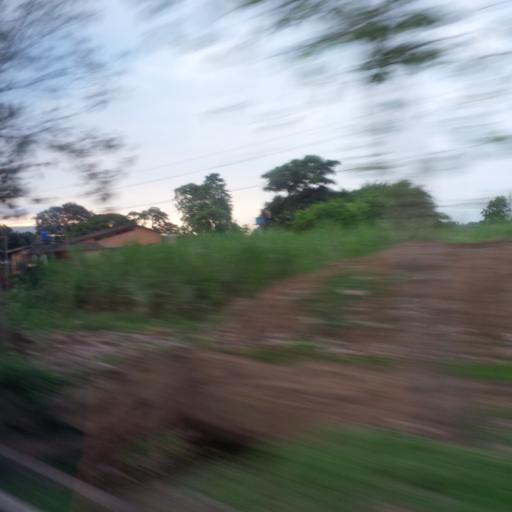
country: EC
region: Guayas
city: Coronel Marcelino Mariduena
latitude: -2.3301
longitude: -79.4230
